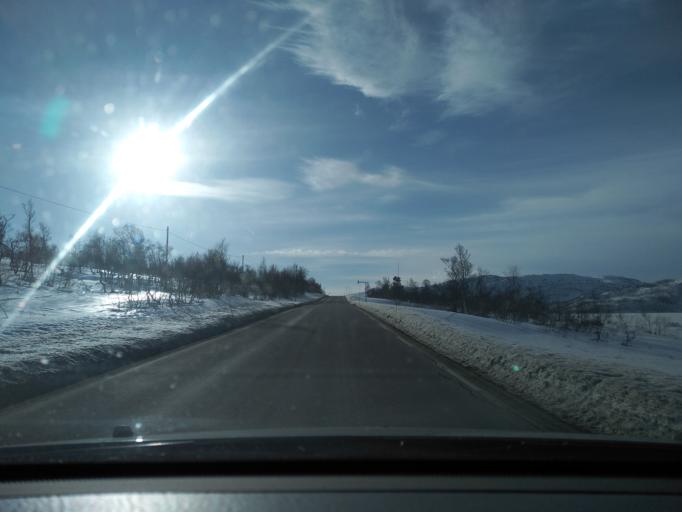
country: NO
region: Aust-Agder
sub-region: Bykle
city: Hovden
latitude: 59.6519
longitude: 7.4804
